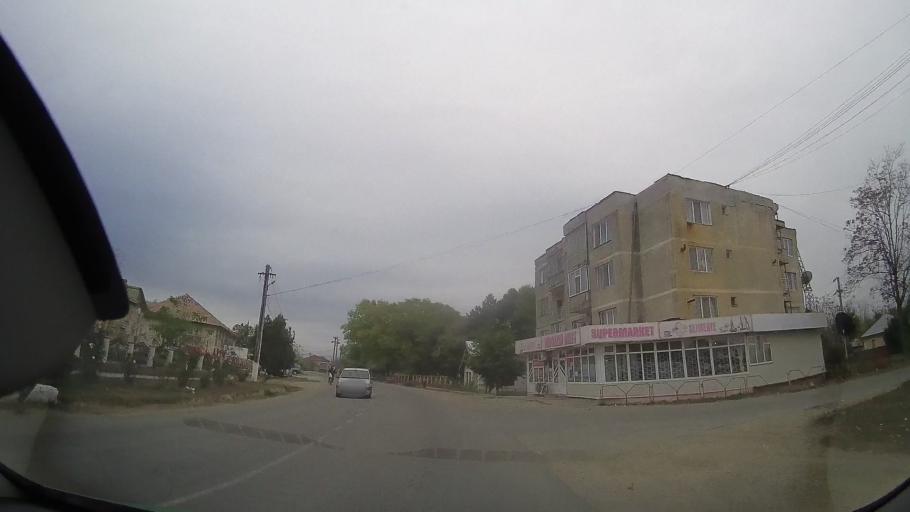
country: RO
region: Ialomita
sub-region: Comuna Grivita
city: Grivita
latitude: 44.7359
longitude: 27.2892
